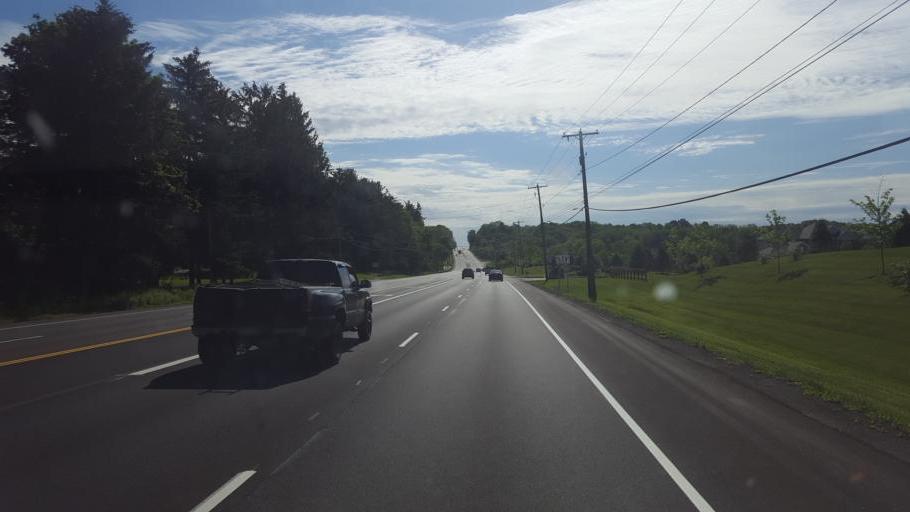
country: US
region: Ohio
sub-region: Summit County
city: Montrose-Ghent
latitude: 41.1358
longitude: -81.6819
